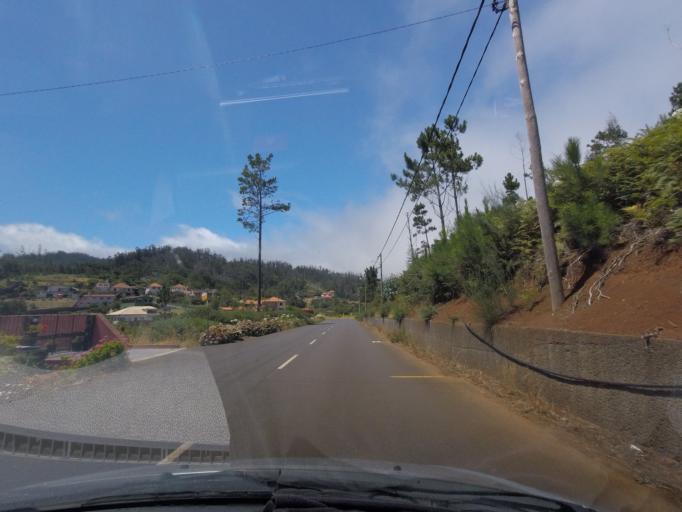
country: PT
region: Madeira
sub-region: Santa Cruz
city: Camacha
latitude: 32.6930
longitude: -16.8344
